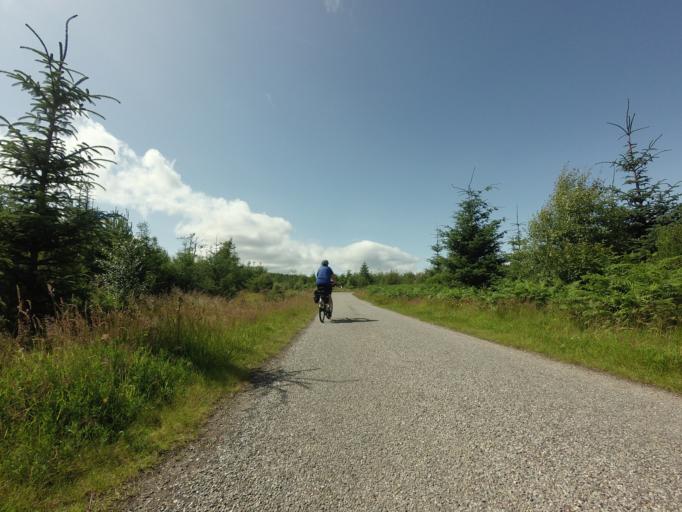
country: GB
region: Scotland
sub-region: Highland
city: Nairn
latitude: 57.4964
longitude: -3.9634
